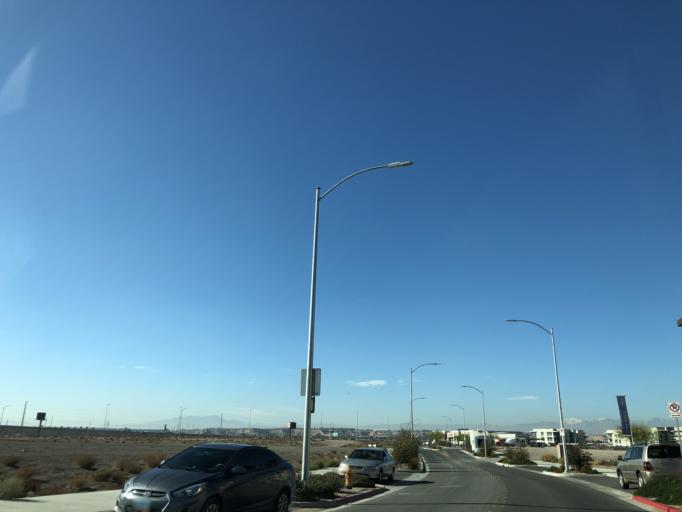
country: US
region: Nevada
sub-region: Clark County
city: Whitney
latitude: 36.0756
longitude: -115.0306
